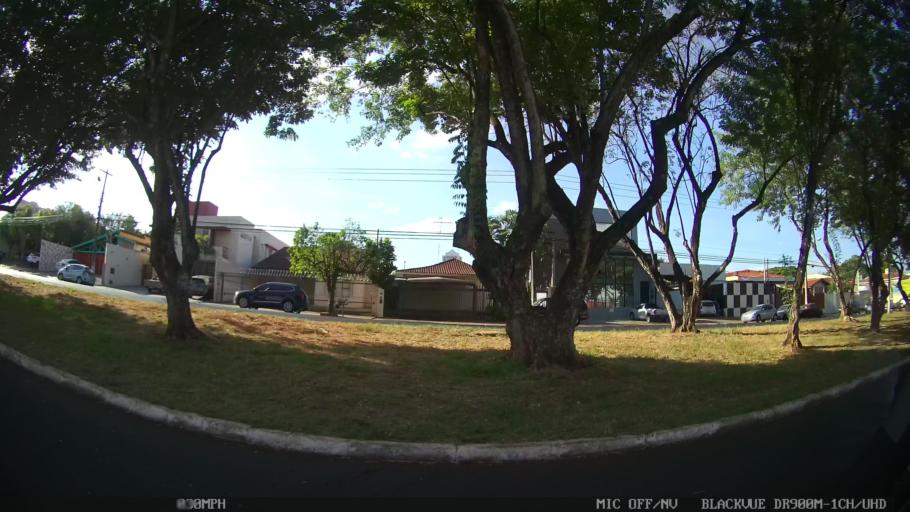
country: BR
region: Sao Paulo
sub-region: Ribeirao Preto
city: Ribeirao Preto
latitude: -21.2049
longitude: -47.7735
